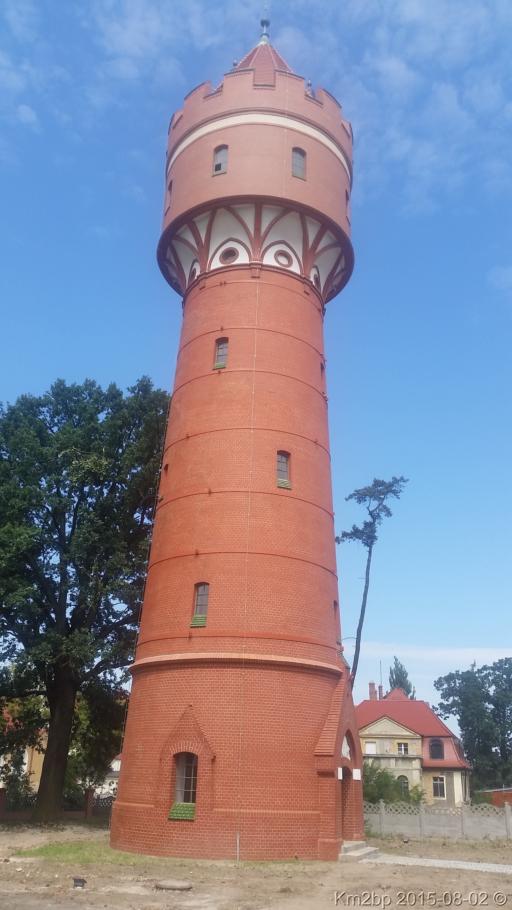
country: PL
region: Lubusz
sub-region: Powiat nowosolski
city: Kozuchow
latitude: 51.7415
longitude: 15.5966
